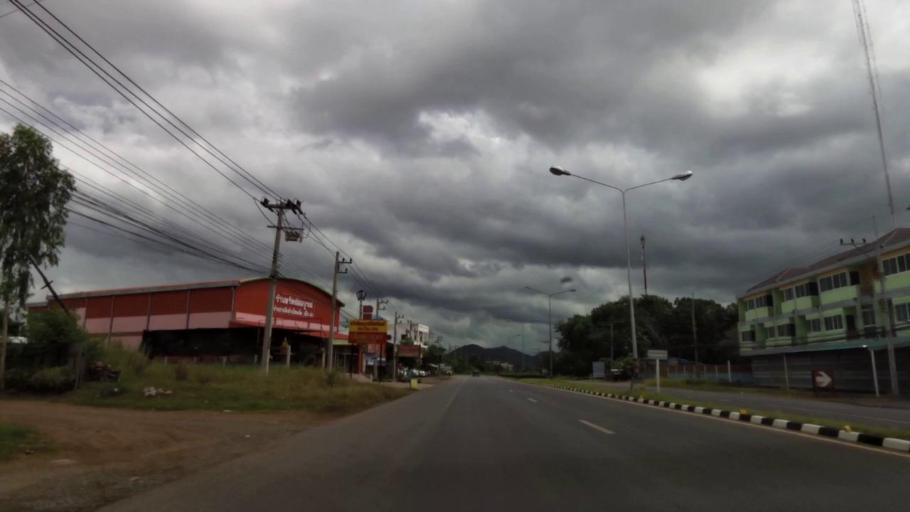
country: TH
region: Nakhon Sawan
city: Phai Sali
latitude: 15.5939
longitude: 100.6476
